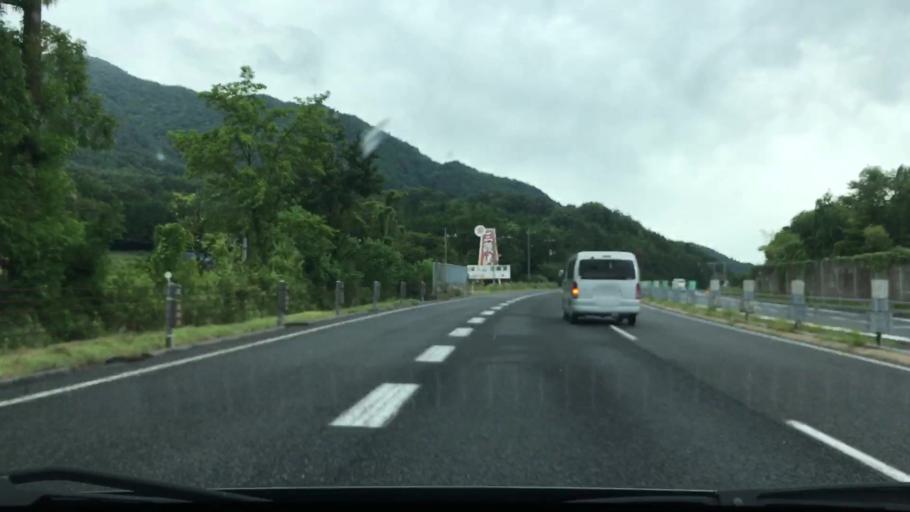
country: JP
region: Hiroshima
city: Hiroshima-shi
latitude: 34.6338
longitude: 132.5140
